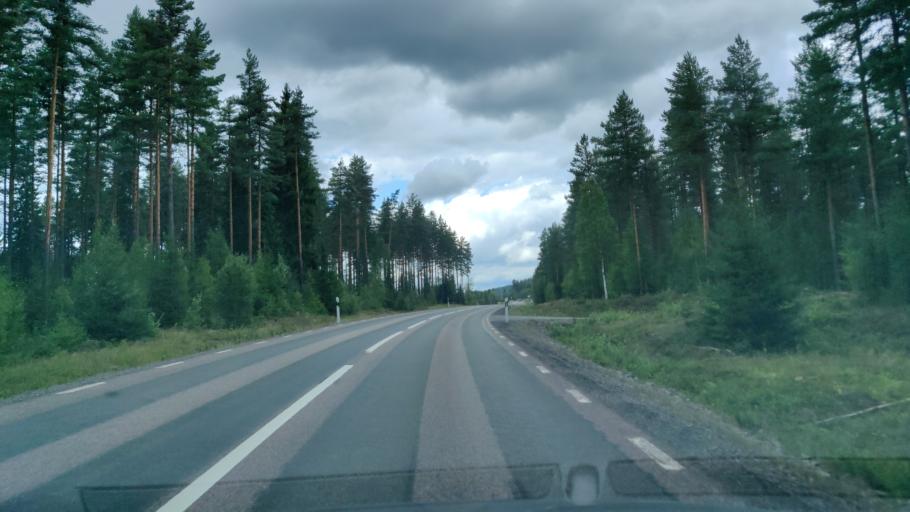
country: SE
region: Vaermland
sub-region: Torsby Kommun
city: Torsby
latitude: 60.5345
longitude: 13.1233
